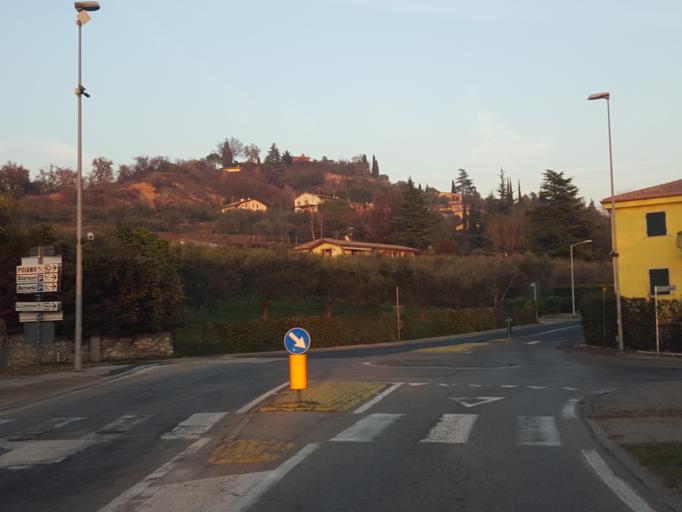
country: IT
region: Veneto
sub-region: Provincia di Verona
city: Garda
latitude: 45.5831
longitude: 10.7256
